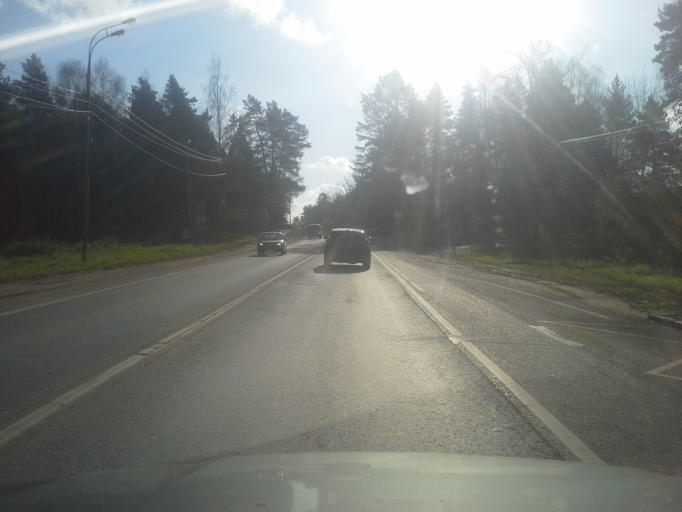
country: RU
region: Moskovskaya
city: Bol'shiye Vyazemy
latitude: 55.6488
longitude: 36.9727
